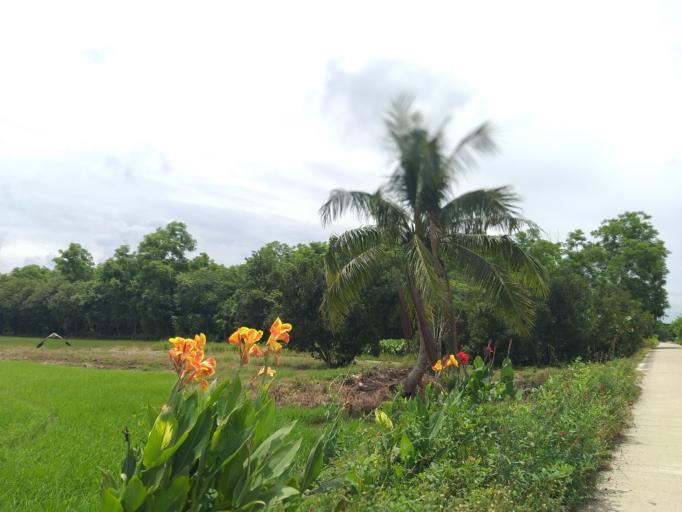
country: TH
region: Pathum Thani
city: Ban Lam Luk Ka
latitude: 14.0317
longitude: 100.8660
